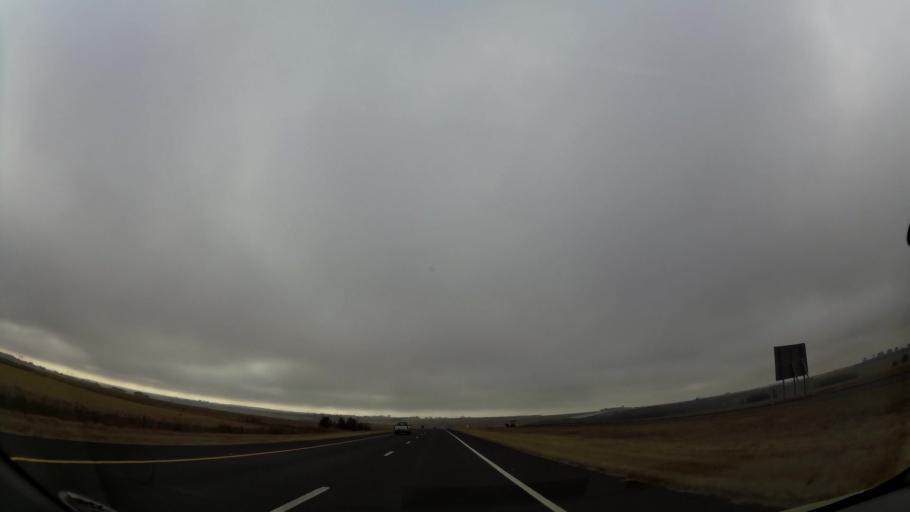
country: ZA
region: Mpumalanga
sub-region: Nkangala District Municipality
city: Delmas
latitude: -26.0686
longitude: 28.7721
